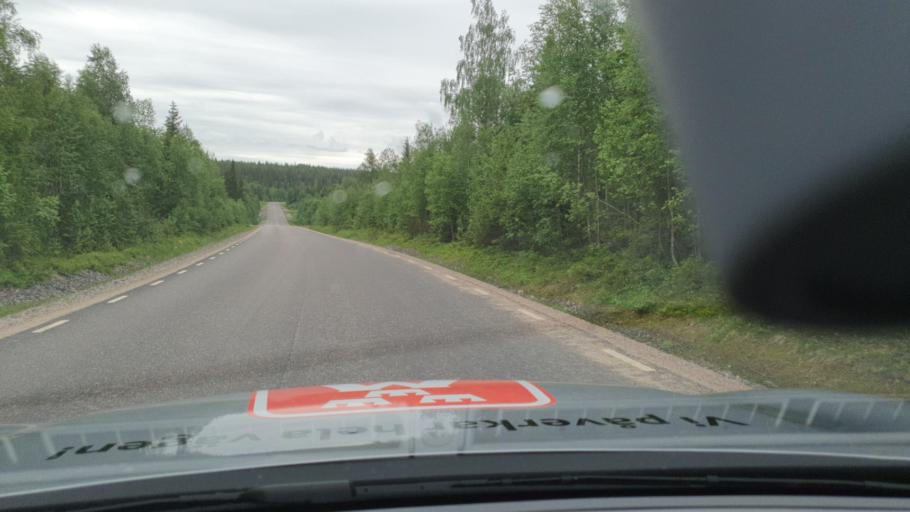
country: SE
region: Norrbotten
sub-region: Overtornea Kommun
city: OEvertornea
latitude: 66.4911
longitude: 23.4452
